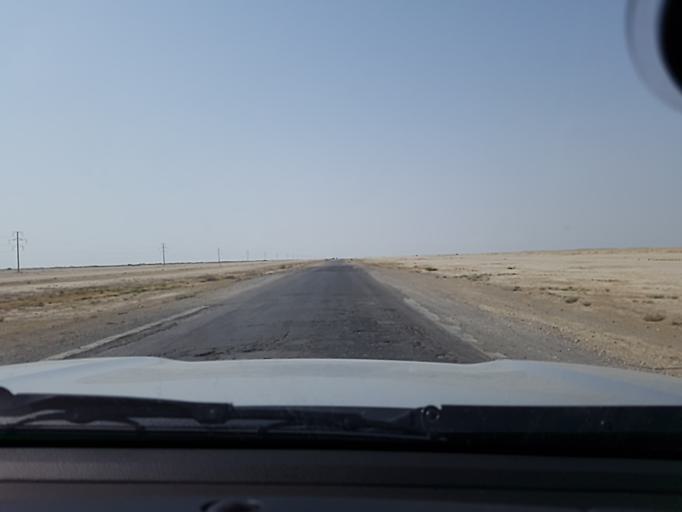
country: TM
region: Balkan
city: Gumdag
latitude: 38.8458
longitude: 54.5957
